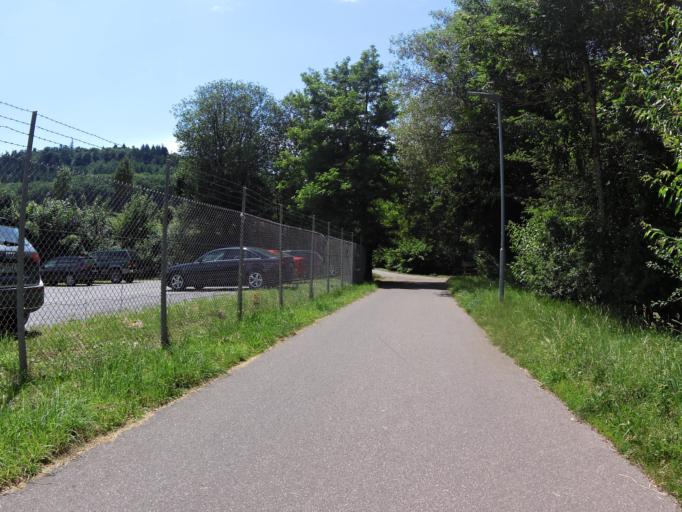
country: DE
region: Baden-Wuerttemberg
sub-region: Freiburg Region
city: Lahr
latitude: 48.3402
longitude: 7.8891
